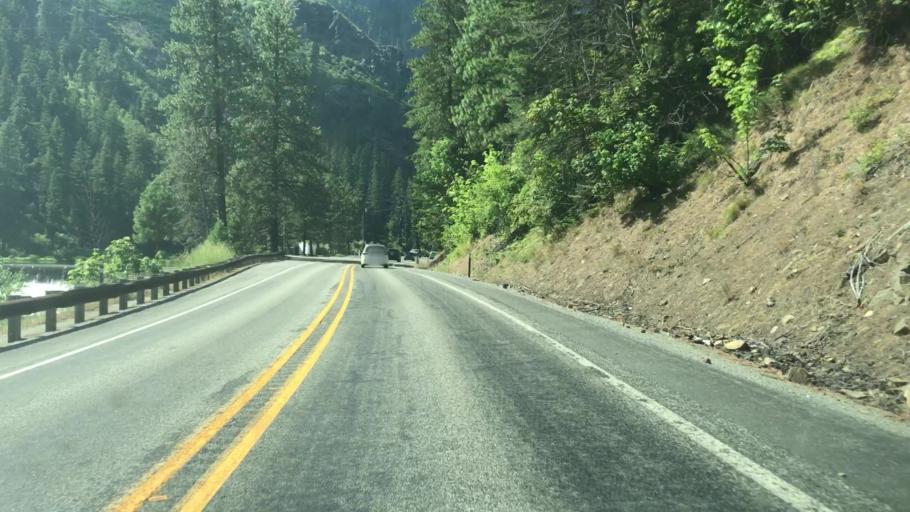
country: US
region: Washington
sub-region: Chelan County
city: Leavenworth
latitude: 47.6164
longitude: -120.7214
